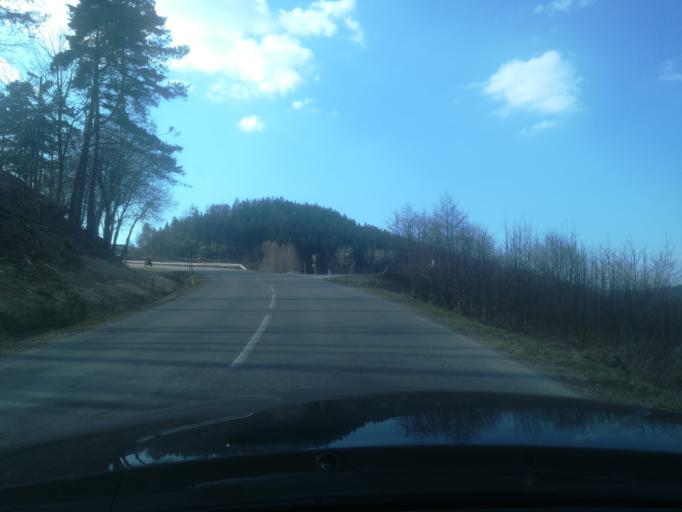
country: AT
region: Upper Austria
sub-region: Politischer Bezirk Freistadt
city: Freistadt
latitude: 48.4458
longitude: 14.6874
